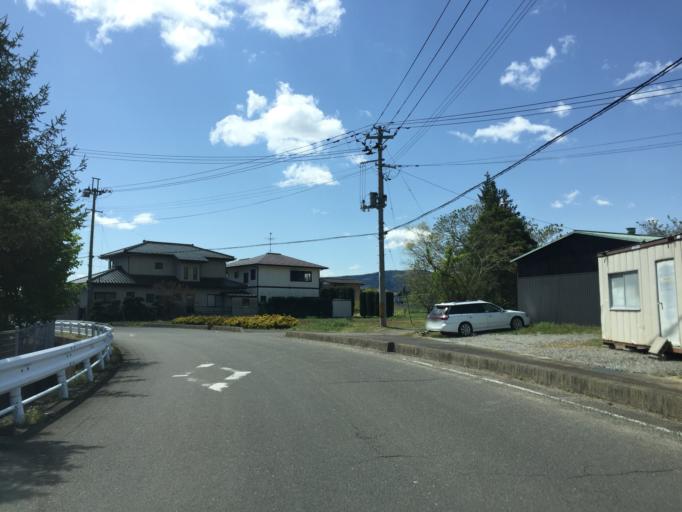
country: JP
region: Fukushima
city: Fukushima-shi
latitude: 37.7378
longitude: 140.3970
